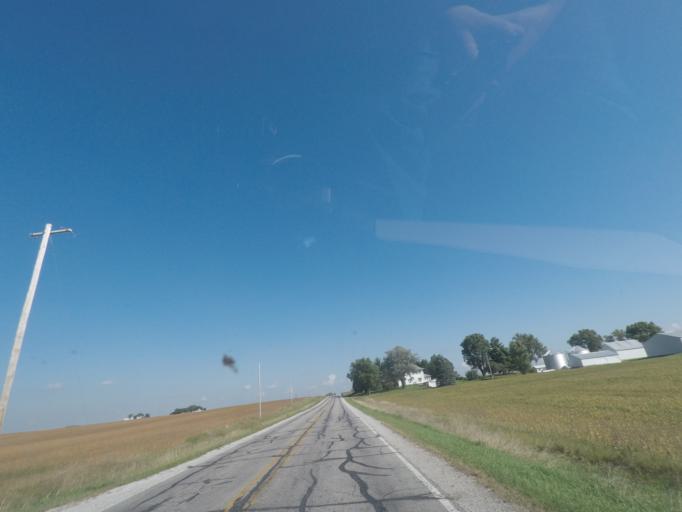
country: US
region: Iowa
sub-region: Story County
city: Nevada
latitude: 42.0247
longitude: -93.4057
